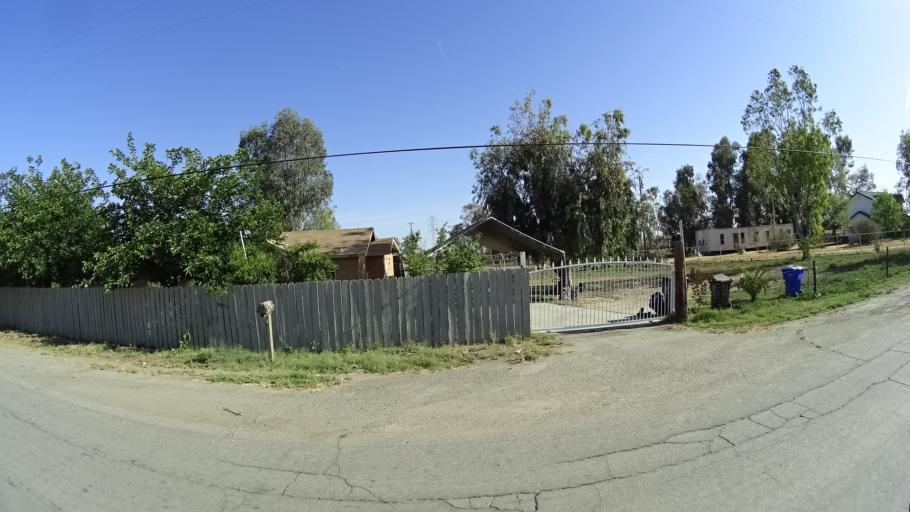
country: US
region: California
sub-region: Kings County
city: Corcoran
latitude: 36.1198
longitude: -119.5646
